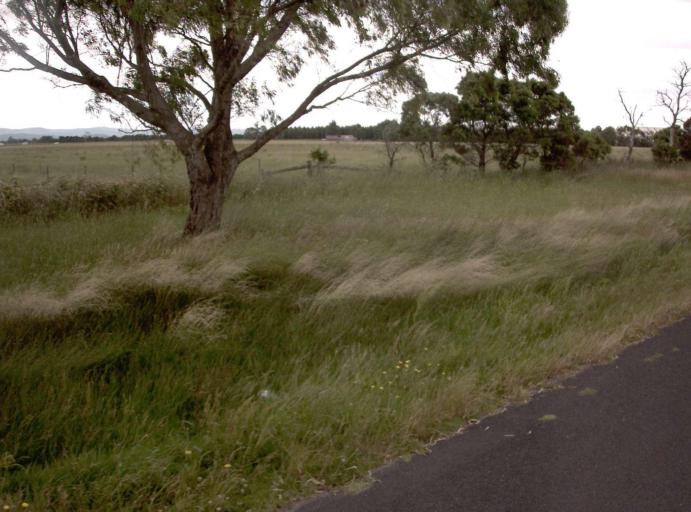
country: AU
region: Victoria
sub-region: Cardinia
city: Koo-Wee-Rup
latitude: -38.2139
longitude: 145.4880
